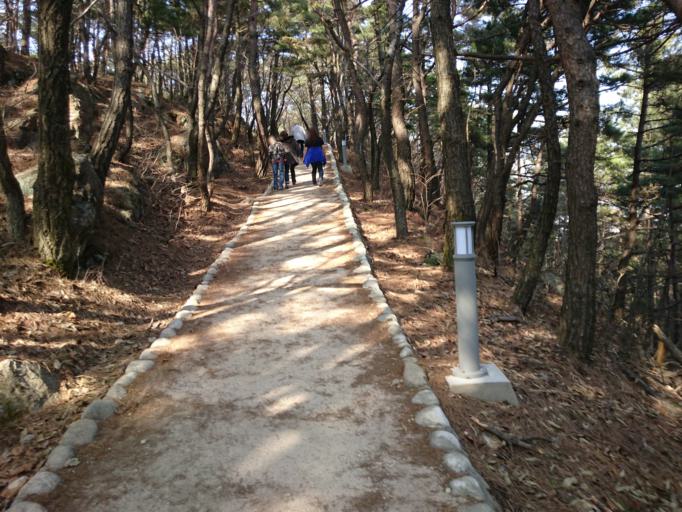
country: KR
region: Daegu
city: Daegu
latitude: 35.8233
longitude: 128.5792
